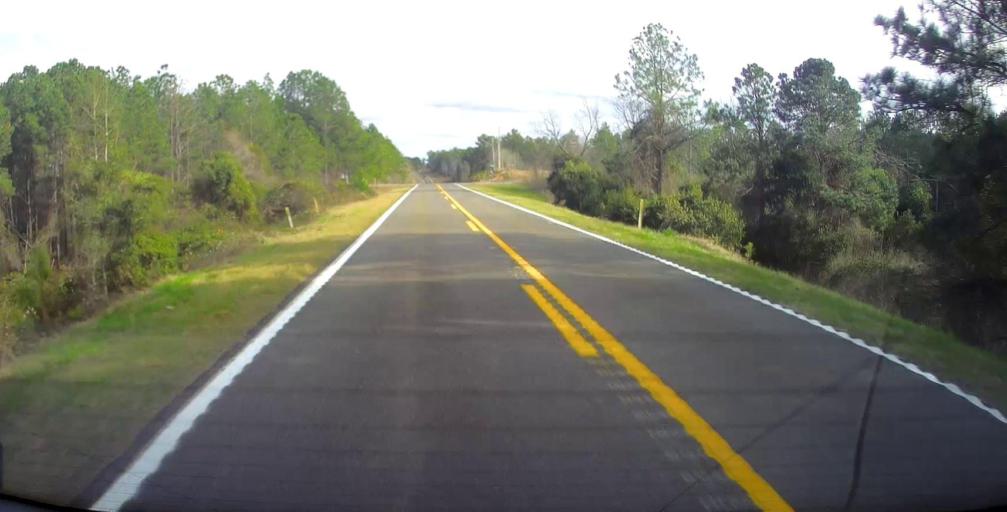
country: US
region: Georgia
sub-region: Marion County
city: Buena Vista
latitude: 32.4415
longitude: -84.5129
